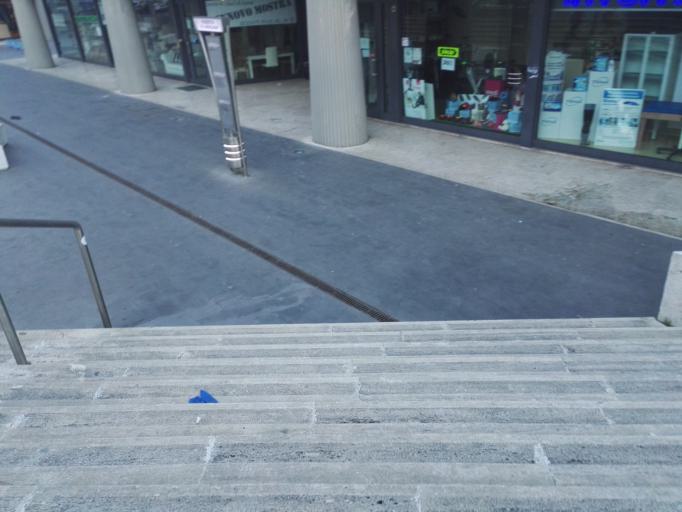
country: IT
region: Latium
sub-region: Citta metropolitana di Roma Capitale
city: Rome
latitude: 41.9092
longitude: 12.5112
